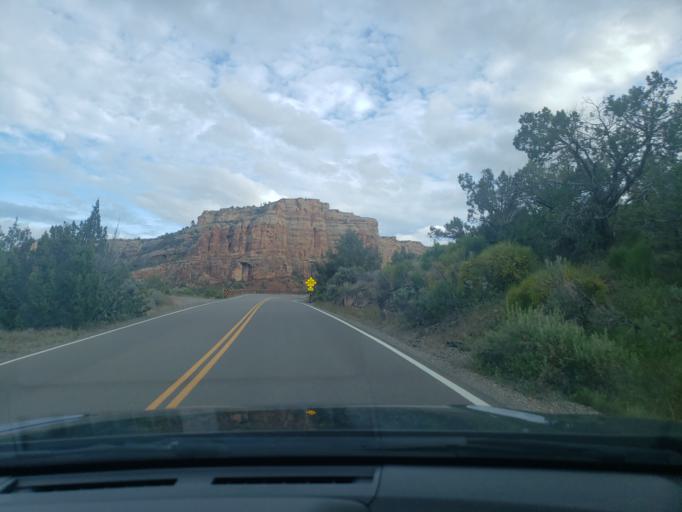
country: US
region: Colorado
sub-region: Mesa County
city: Redlands
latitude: 39.0282
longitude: -108.6360
